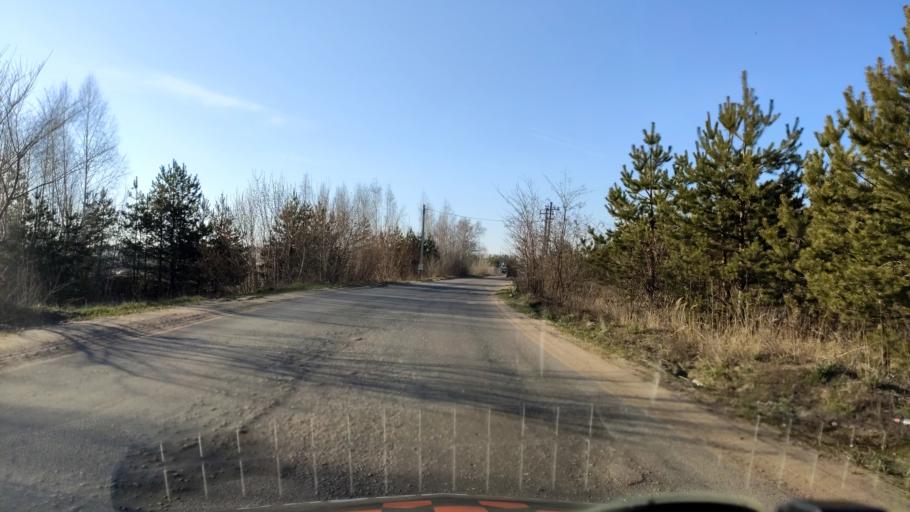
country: RU
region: Voronezj
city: Podgornoye
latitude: 51.8283
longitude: 39.2079
